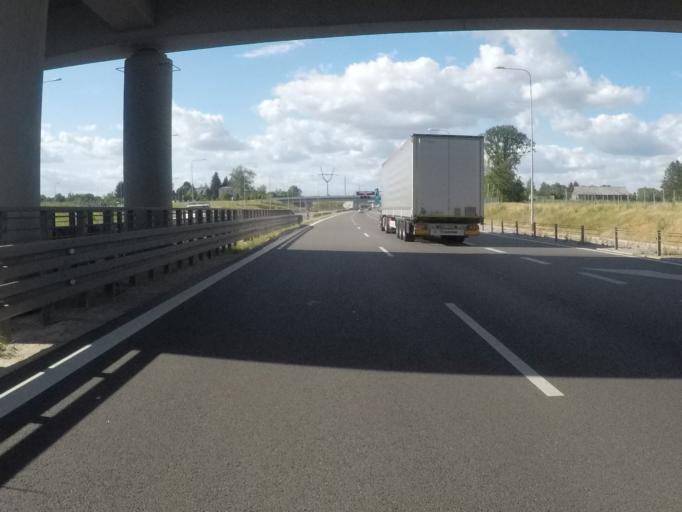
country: PL
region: Lublin Voivodeship
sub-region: Powiat lubelski
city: Kozubszczyzna
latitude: 51.2127
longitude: 22.4419
